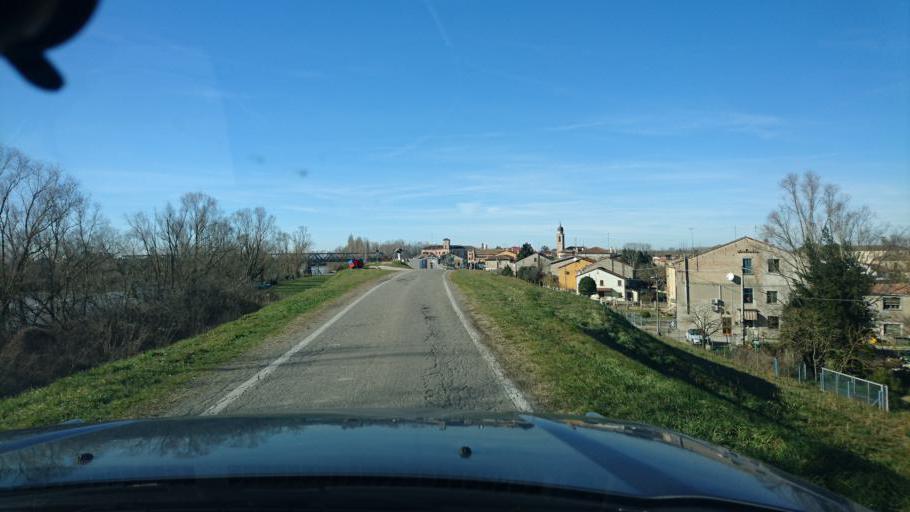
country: IT
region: Veneto
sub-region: Provincia di Rovigo
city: Ariano
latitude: 44.9425
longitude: 12.1255
